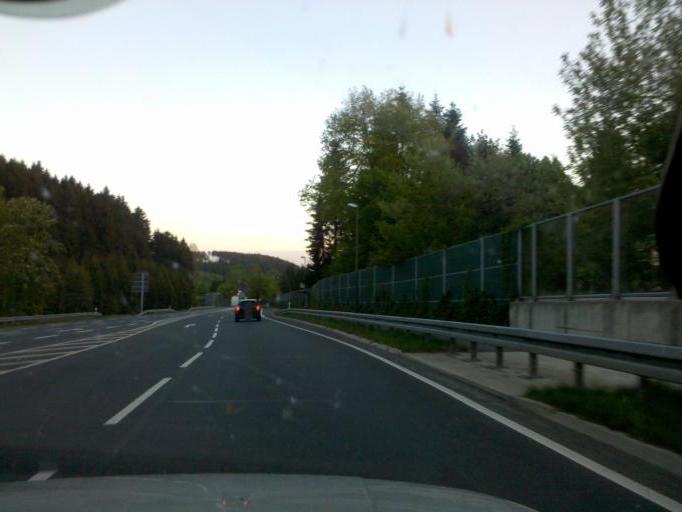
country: DE
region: North Rhine-Westphalia
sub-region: Regierungsbezirk Koln
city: Gummersbach
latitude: 51.0120
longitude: 7.5564
